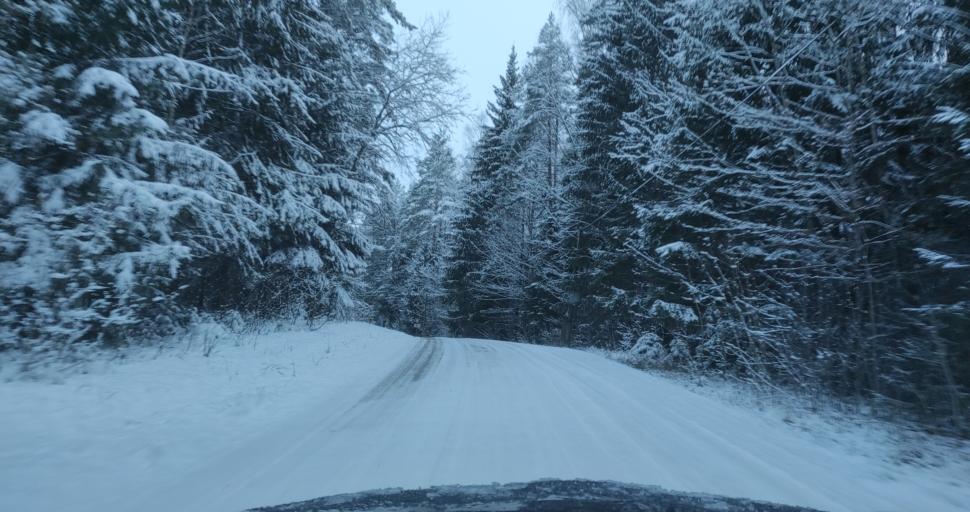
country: LV
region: Alsunga
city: Alsunga
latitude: 56.9612
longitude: 21.6031
